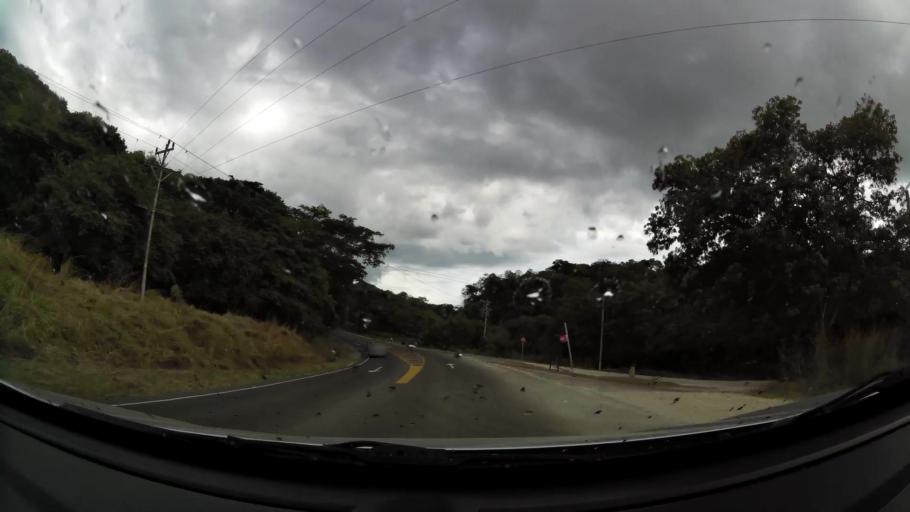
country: CR
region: Guanacaste
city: Nandayure
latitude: 10.2221
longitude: -85.2165
